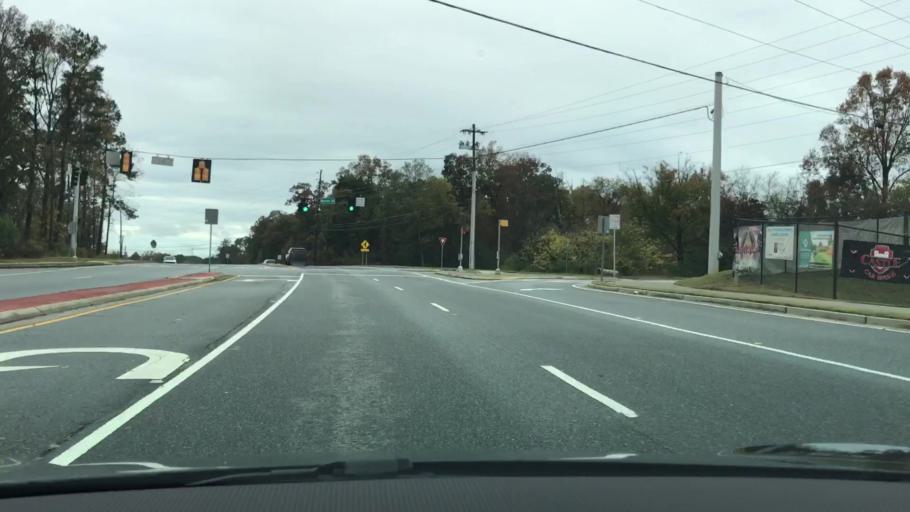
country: US
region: Georgia
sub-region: Gwinnett County
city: Suwanee
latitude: 34.1055
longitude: -84.1429
